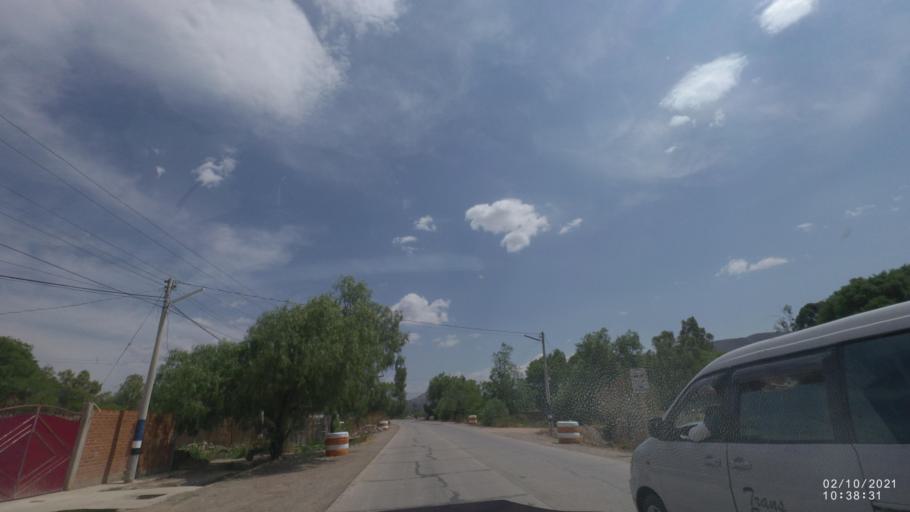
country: BO
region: Cochabamba
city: Capinota
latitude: -17.6336
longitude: -66.2654
